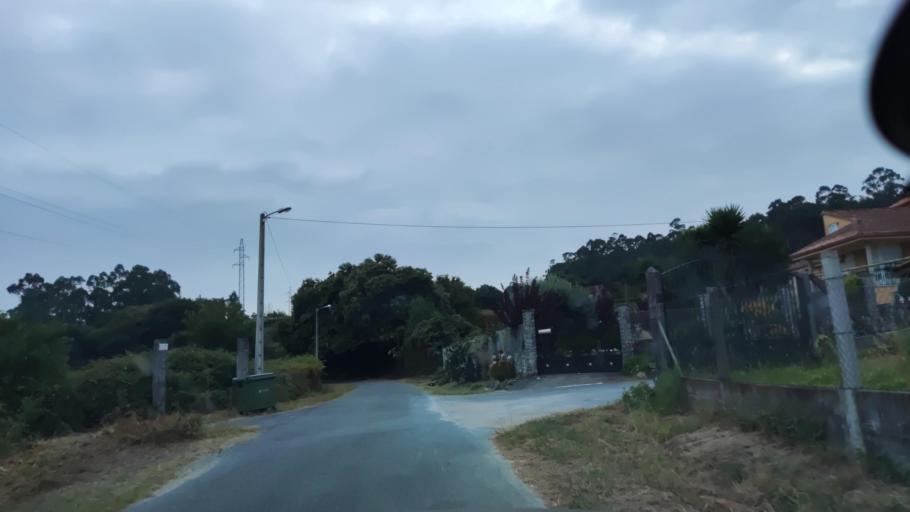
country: ES
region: Galicia
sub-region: Provincia de Pontevedra
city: Catoira
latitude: 42.7093
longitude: -8.7219
